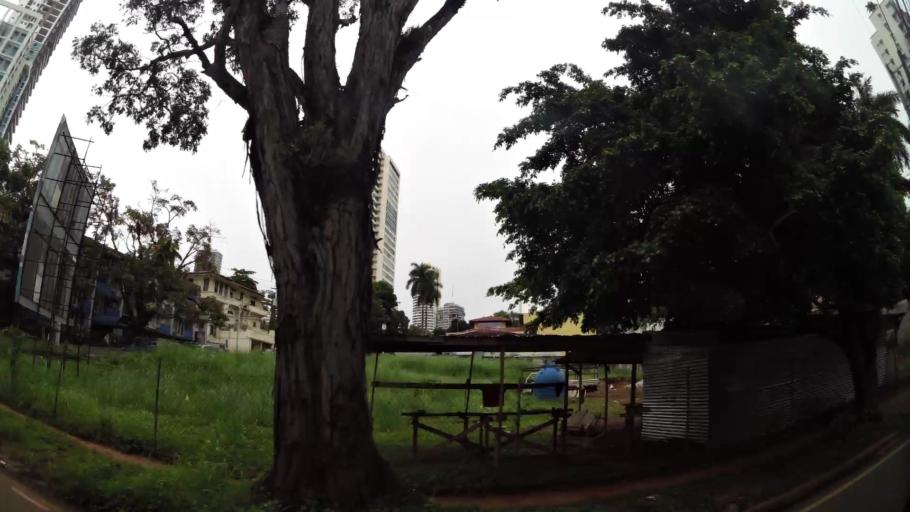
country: PA
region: Panama
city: Panama
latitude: 8.9766
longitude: -79.5282
